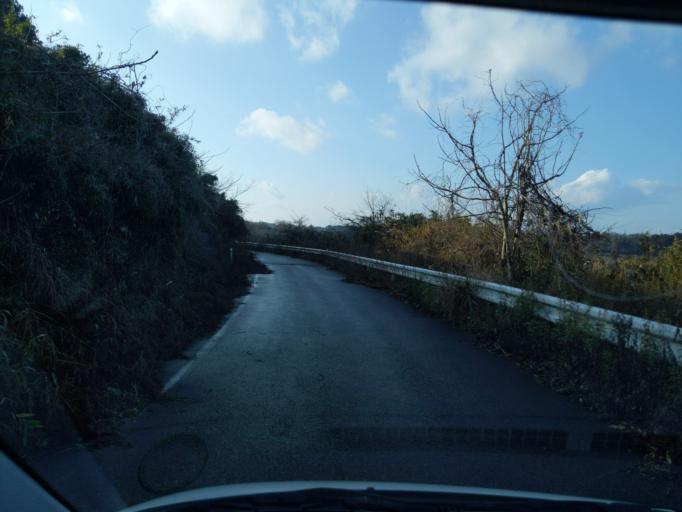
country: JP
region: Miyagi
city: Wakuya
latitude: 38.6880
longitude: 141.1182
